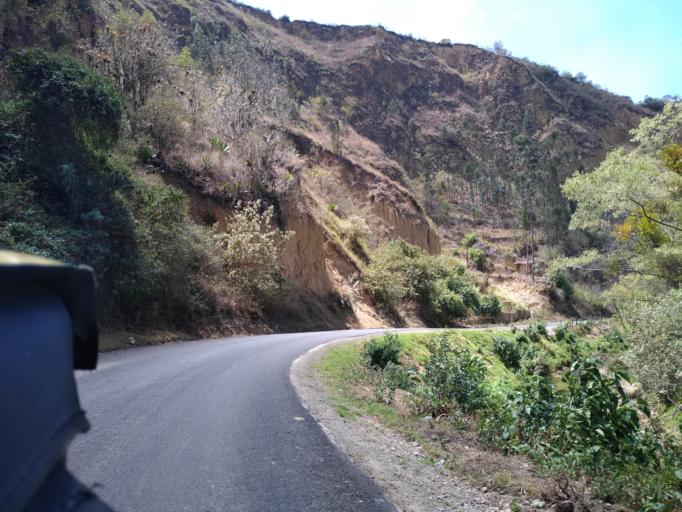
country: PE
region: Amazonas
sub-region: Provincia de Chachapoyas
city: Duraznopampa
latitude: -6.5769
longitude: -77.8256
